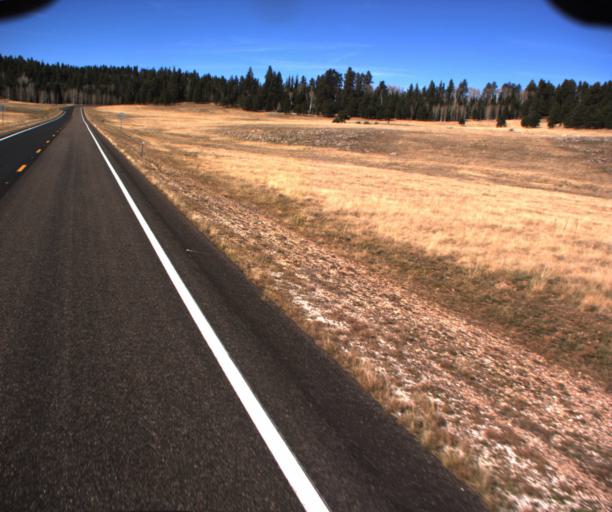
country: US
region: Arizona
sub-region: Coconino County
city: Grand Canyon
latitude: 36.5008
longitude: -112.1369
